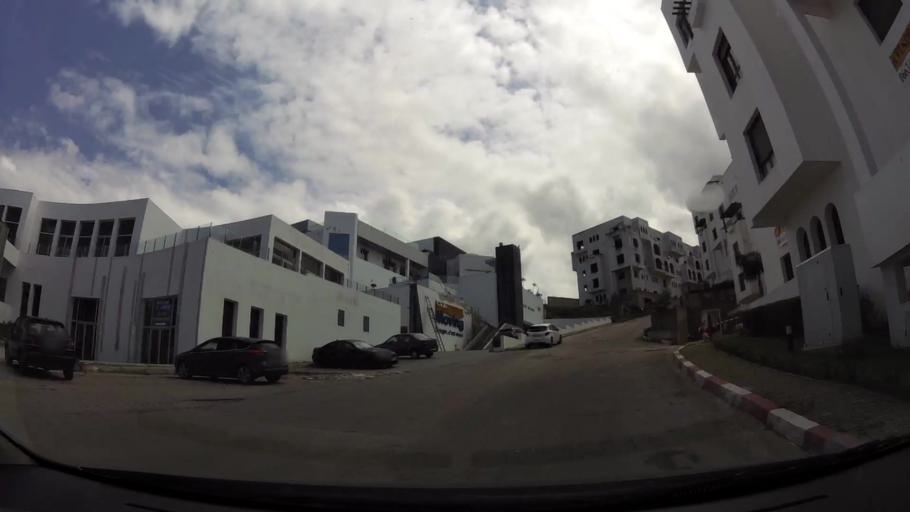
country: MA
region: Tanger-Tetouan
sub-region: Tanger-Assilah
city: Tangier
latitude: 35.7813
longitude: -5.7599
